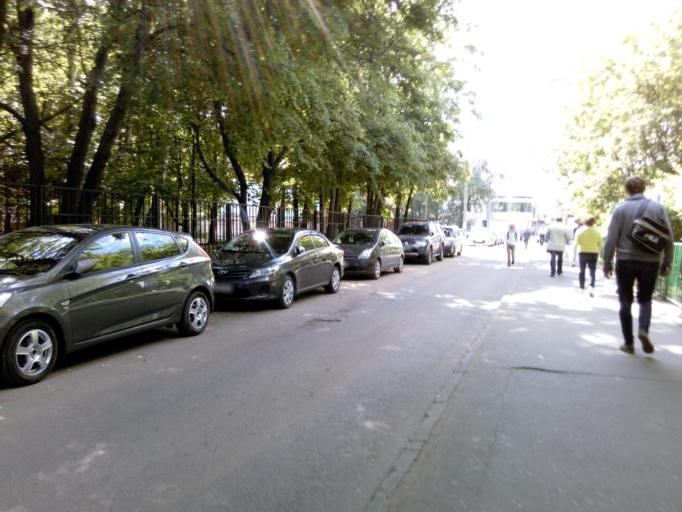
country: RU
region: Moskovskaya
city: Levoberezhnyy
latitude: 55.8571
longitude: 37.4749
